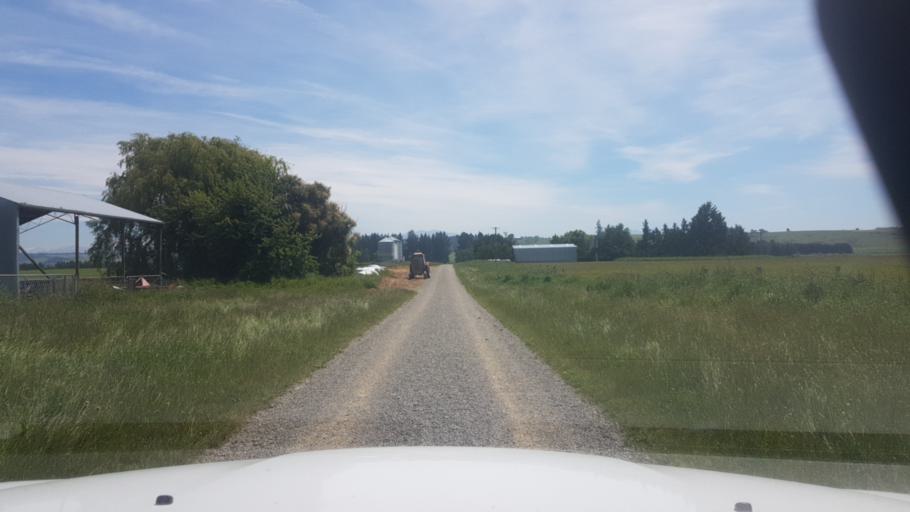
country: NZ
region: Canterbury
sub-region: Timaru District
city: Pleasant Point
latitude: -44.2263
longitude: 171.1648
